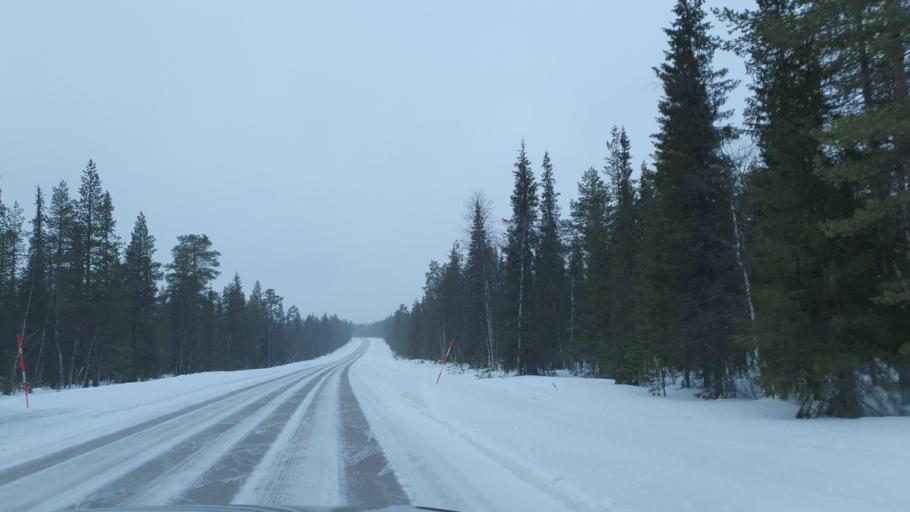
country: FI
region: Lapland
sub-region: Tunturi-Lappi
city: Kolari
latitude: 67.4933
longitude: 23.8946
